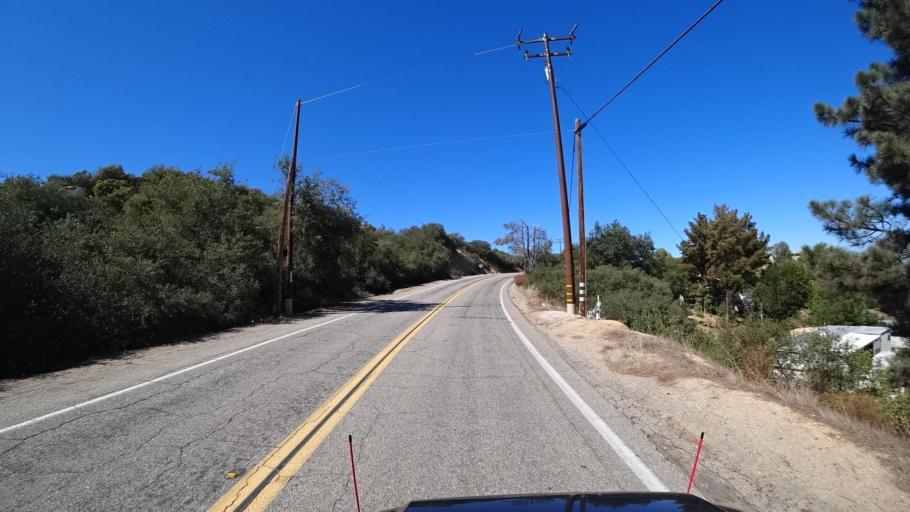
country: US
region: California
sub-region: San Diego County
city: Alpine
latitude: 32.7253
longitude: -116.7662
